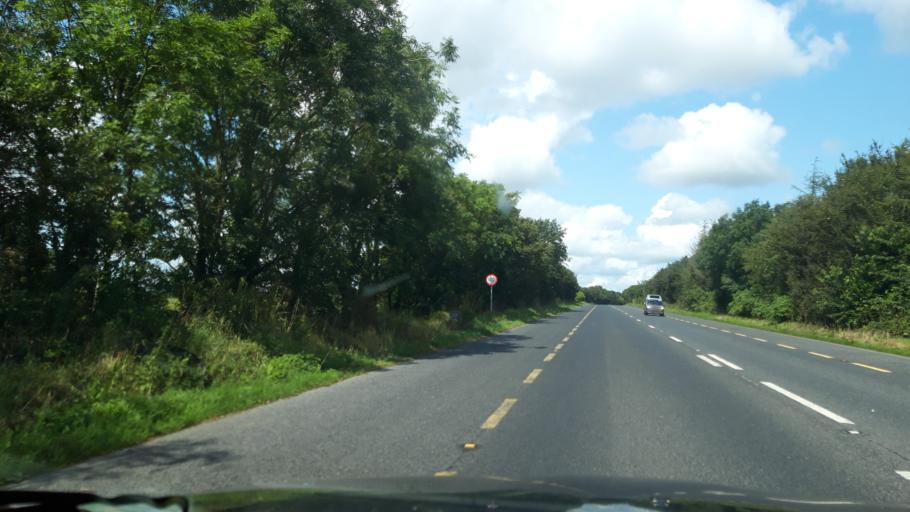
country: IE
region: Munster
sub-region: Waterford
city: Waterford
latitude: 52.2731
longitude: -7.0493
